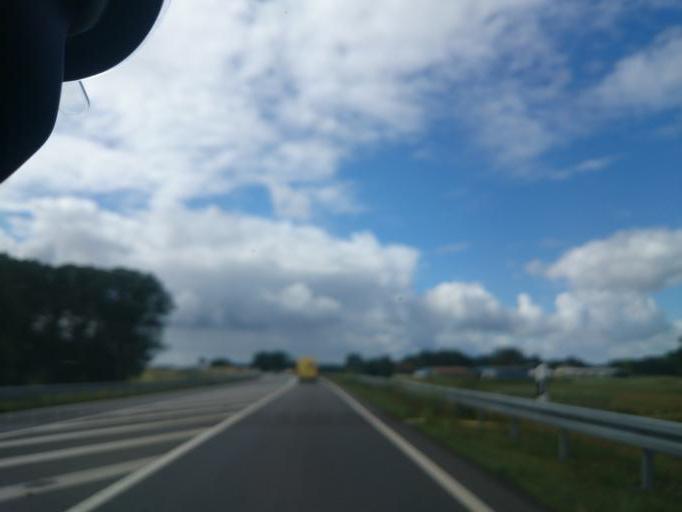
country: DE
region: Mecklenburg-Vorpommern
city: Samtens
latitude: 54.3570
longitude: 13.3080
